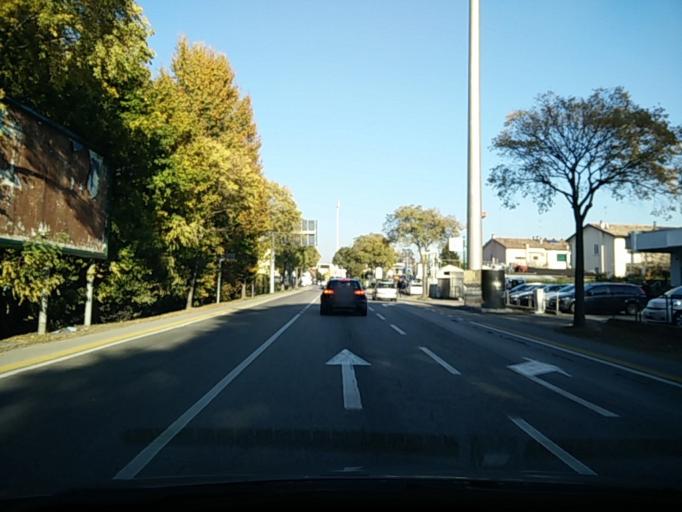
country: IT
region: Veneto
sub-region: Provincia di Treviso
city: Treviso
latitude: 45.6714
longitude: 12.2303
